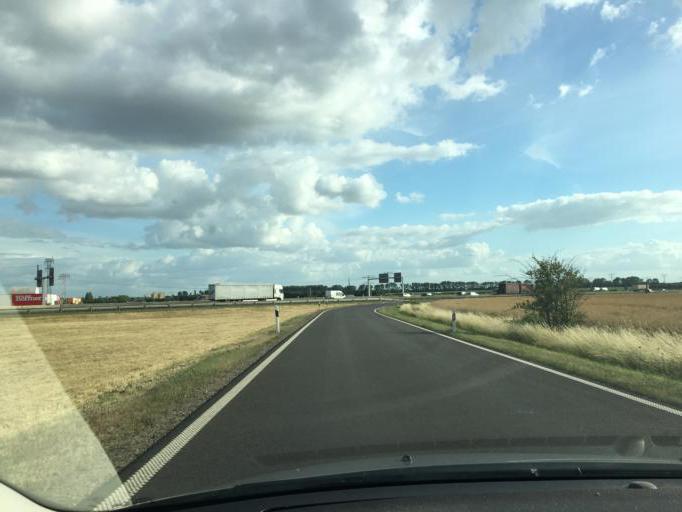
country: DE
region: Saxony-Anhalt
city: Barleben
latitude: 52.1867
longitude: 11.6142
